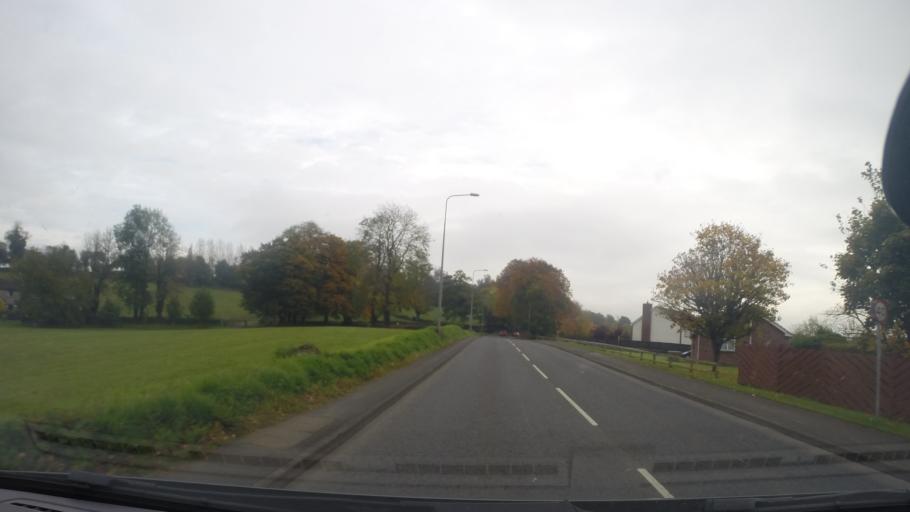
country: GB
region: Northern Ireland
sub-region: Fermanagh District
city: Enniskillen
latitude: 54.3533
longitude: -7.6604
